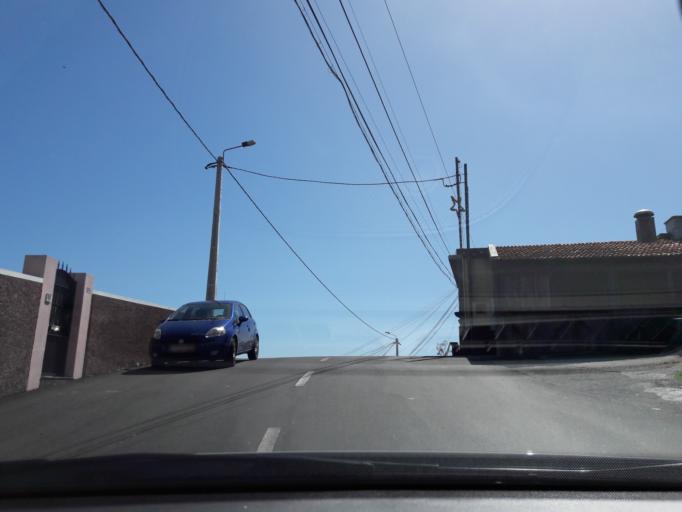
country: PT
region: Madeira
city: Camara de Lobos
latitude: 32.6740
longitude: -16.9542
